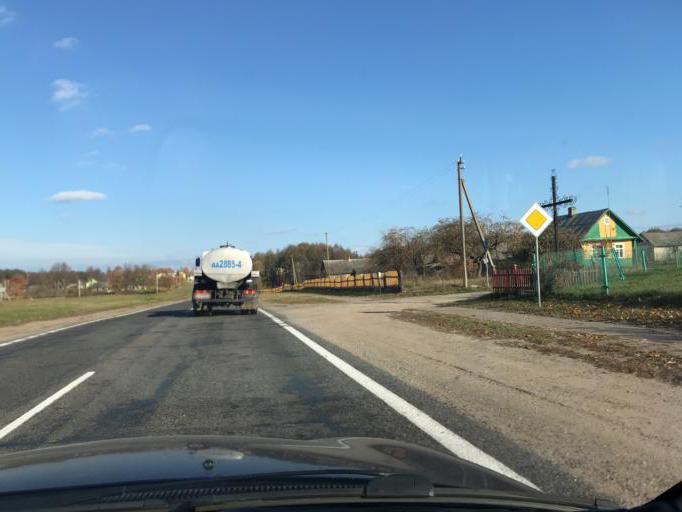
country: BY
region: Grodnenskaya
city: Lida
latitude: 54.0159
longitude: 25.2190
